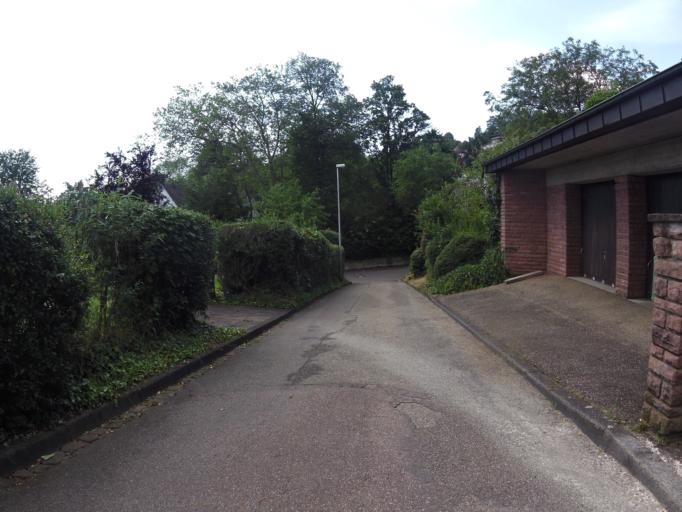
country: DE
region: Baden-Wuerttemberg
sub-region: Freiburg Region
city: Lahr
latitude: 48.3445
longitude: 7.8616
